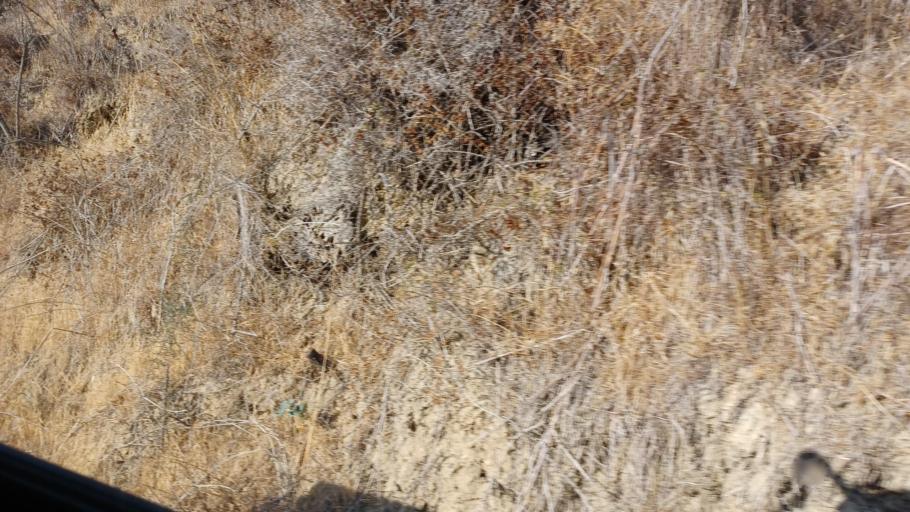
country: CY
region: Pafos
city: Tala
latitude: 34.9258
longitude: 32.4954
